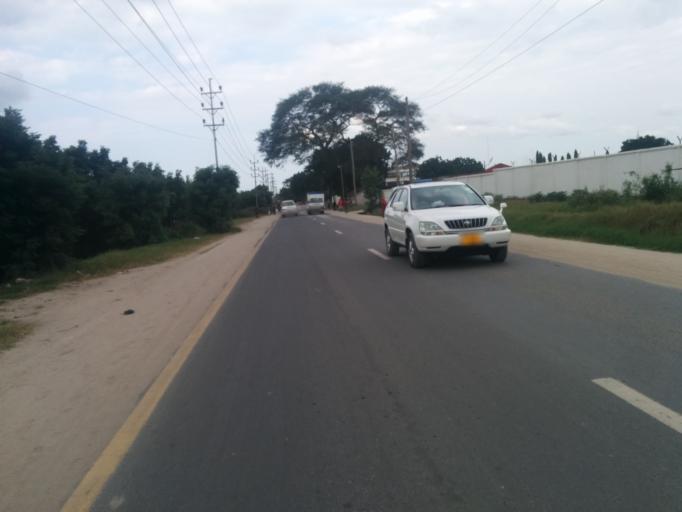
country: TZ
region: Dar es Salaam
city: Dar es Salaam
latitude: -6.8302
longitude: 39.2737
